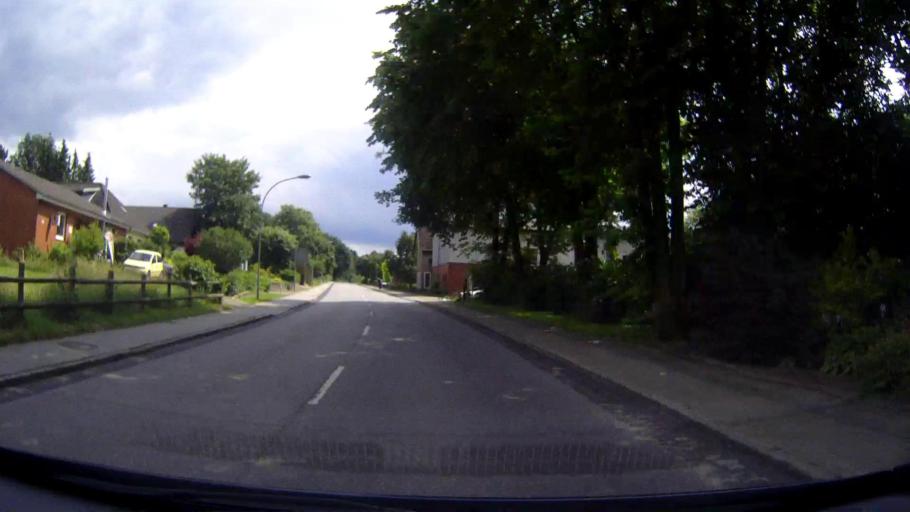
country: DE
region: Schleswig-Holstein
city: Seefeld
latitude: 54.1080
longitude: 9.4714
